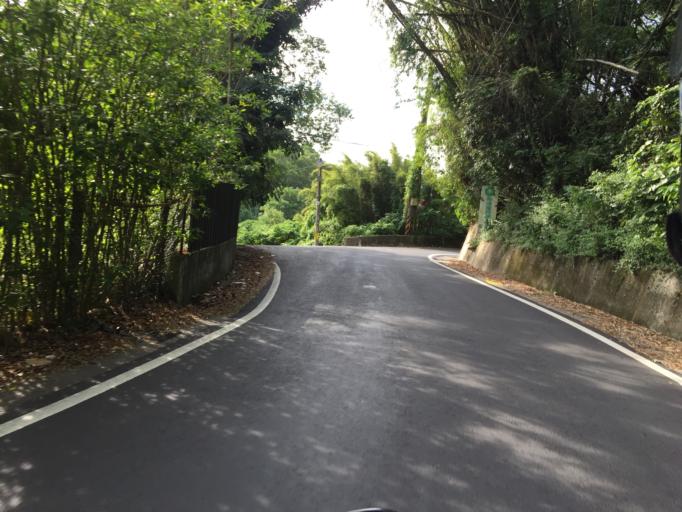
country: TW
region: Taiwan
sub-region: Hsinchu
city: Hsinchu
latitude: 24.7672
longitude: 120.9391
